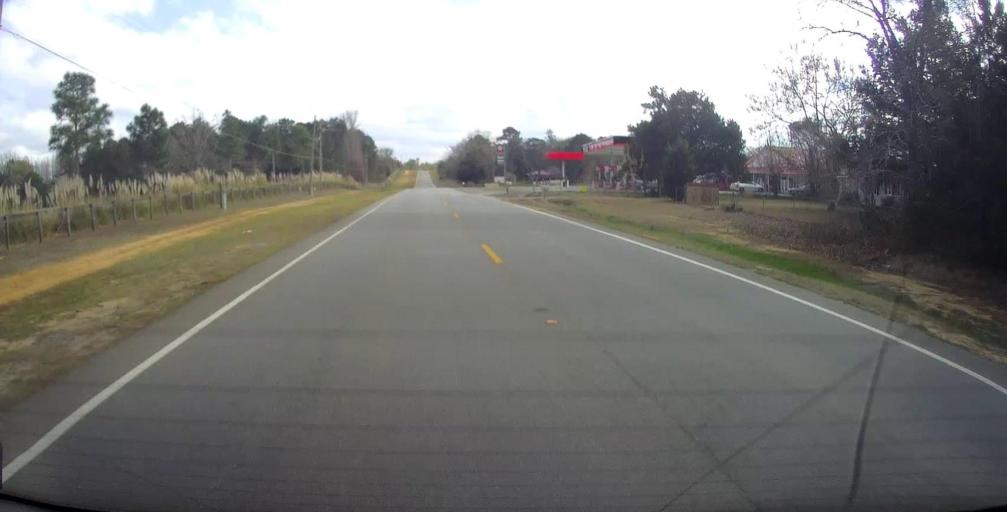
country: US
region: Georgia
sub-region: Marion County
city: Buena Vista
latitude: 32.4574
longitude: -84.5374
